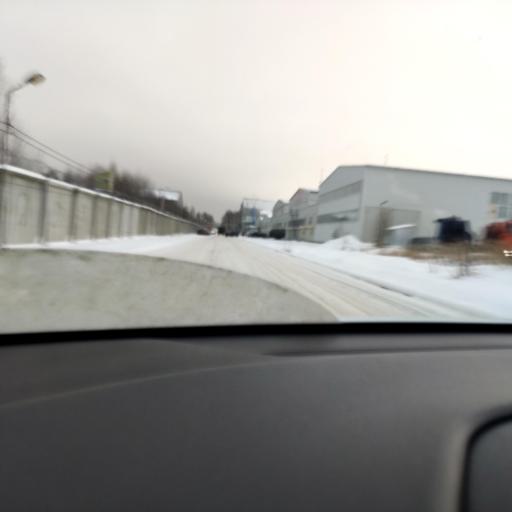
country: RU
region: Tatarstan
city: Osinovo
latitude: 55.8898
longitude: 48.8324
